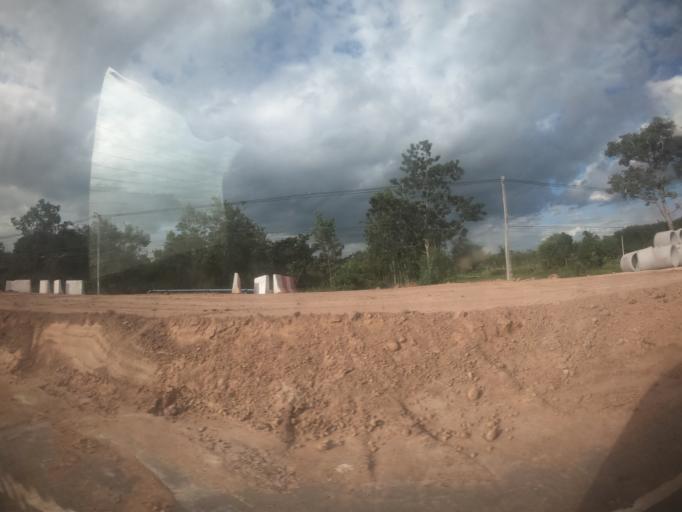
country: TH
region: Surin
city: Kap Choeng
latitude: 14.4960
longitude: 103.5684
